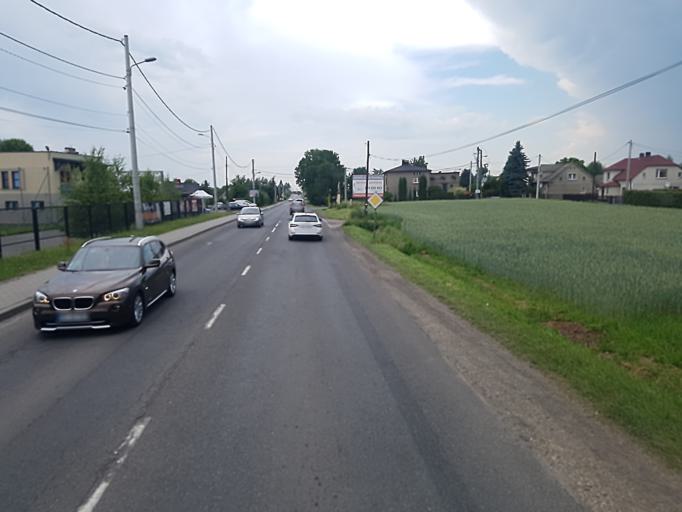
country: PL
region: Silesian Voivodeship
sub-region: Powiat wodzislawski
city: Mszana
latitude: 49.9874
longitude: 18.5023
